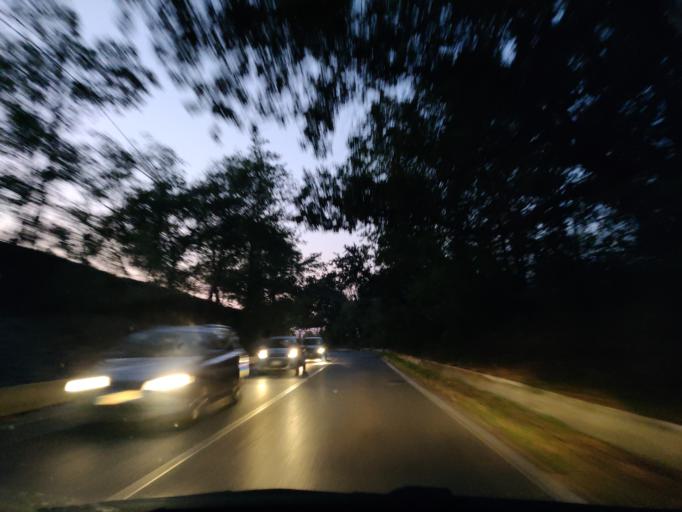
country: IT
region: Latium
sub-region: Citta metropolitana di Roma Capitale
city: Npp 23 (Parco Leonardo)
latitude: 41.8425
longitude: 12.2737
